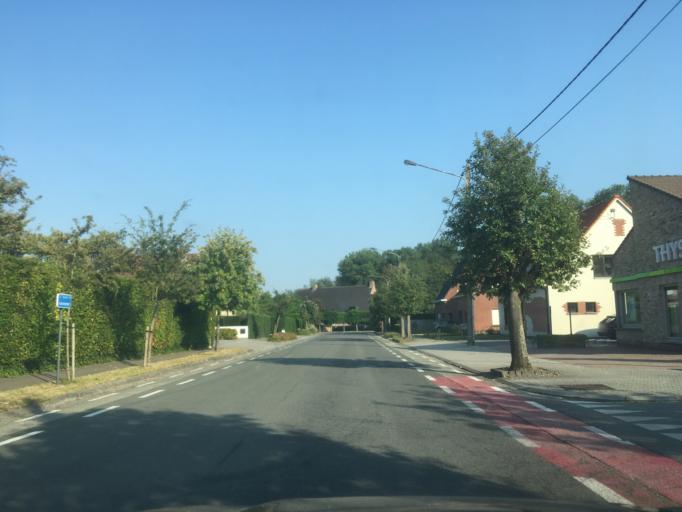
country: BE
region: Flanders
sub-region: Provincie West-Vlaanderen
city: Oostrozebeke
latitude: 50.8908
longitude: 3.3348
